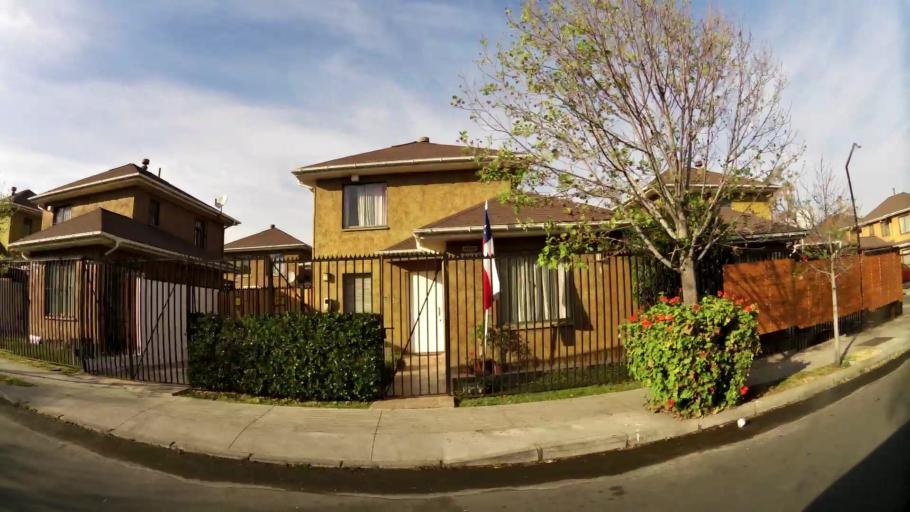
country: CL
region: Santiago Metropolitan
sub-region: Provincia de Cordillera
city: Puente Alto
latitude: -33.5577
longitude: -70.5508
